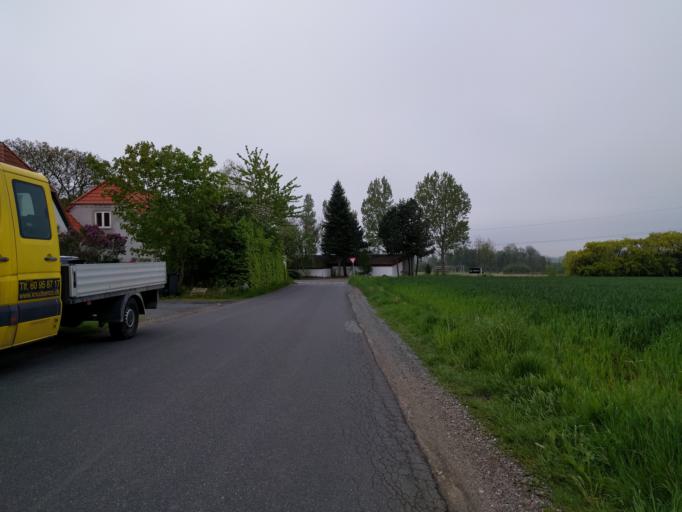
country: DK
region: South Denmark
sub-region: Odense Kommune
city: Bullerup
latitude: 55.3871
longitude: 10.5125
